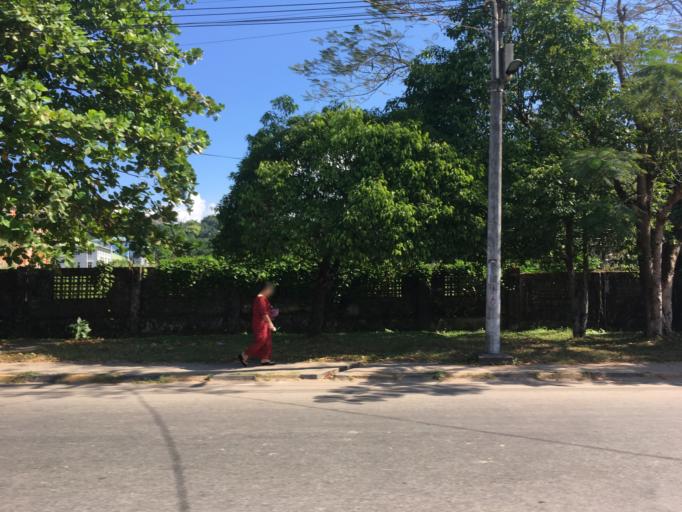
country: MM
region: Mon
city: Mawlamyine
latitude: 16.4649
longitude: 97.6278
